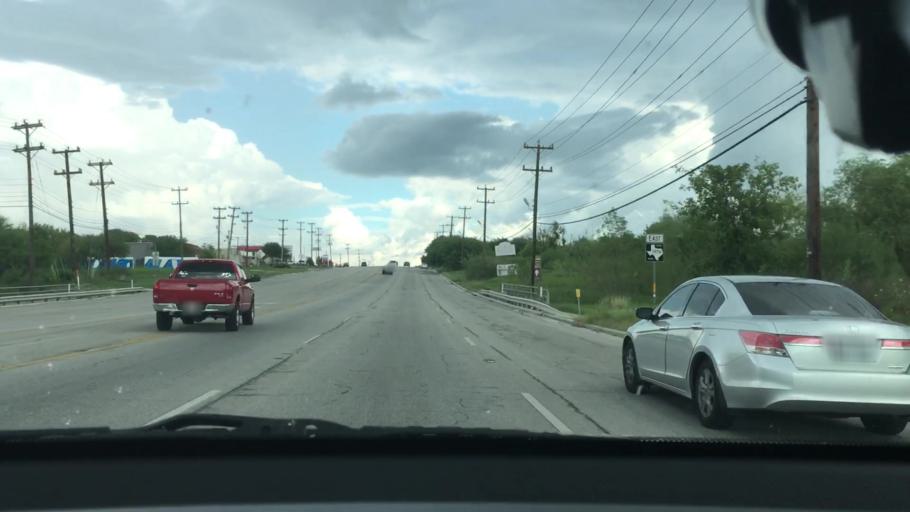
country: US
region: Texas
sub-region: Bexar County
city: Windcrest
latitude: 29.5030
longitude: -98.3665
